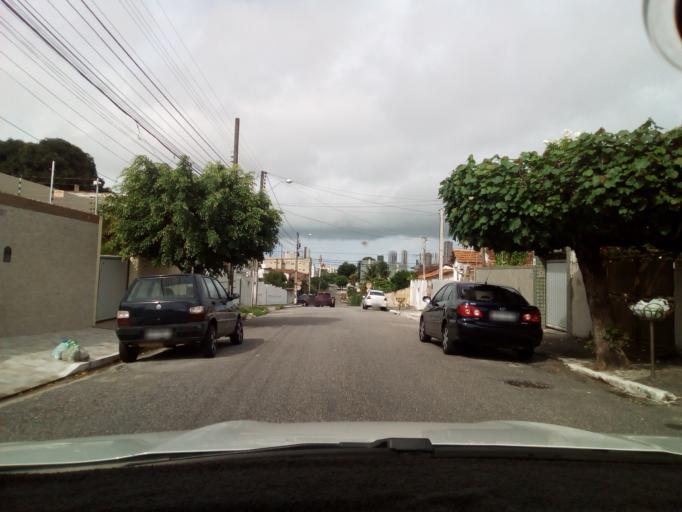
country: BR
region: Paraiba
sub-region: Joao Pessoa
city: Joao Pessoa
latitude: -7.1253
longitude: -34.8542
